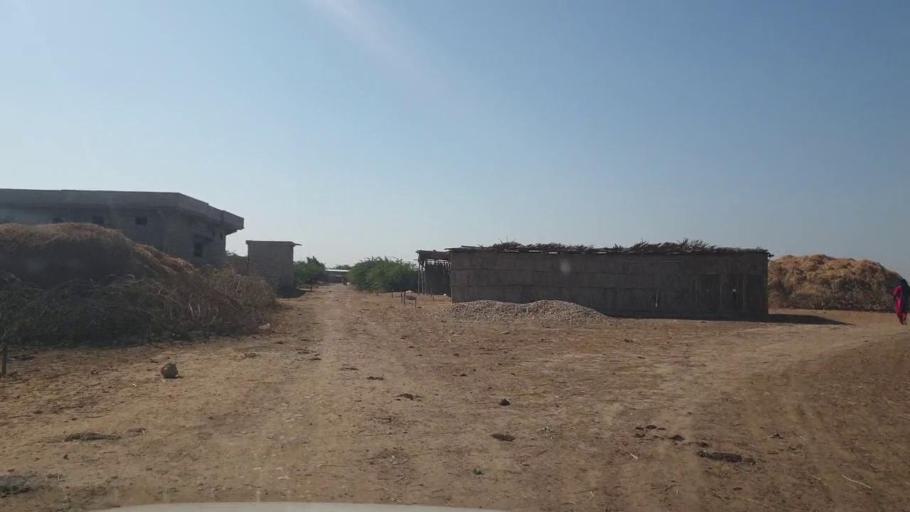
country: PK
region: Sindh
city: Chuhar Jamali
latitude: 24.4378
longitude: 67.8419
